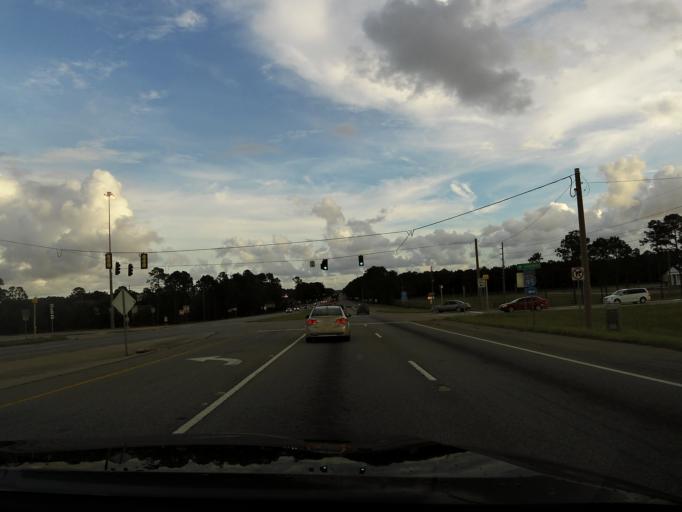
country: US
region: Georgia
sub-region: Glynn County
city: Dock Junction
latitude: 31.2402
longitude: -81.5025
